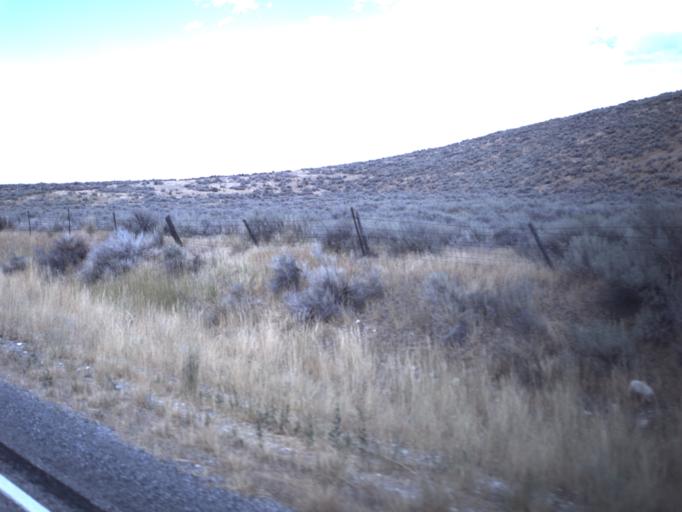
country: US
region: Utah
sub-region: Box Elder County
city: Garland
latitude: 41.7787
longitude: -112.0940
